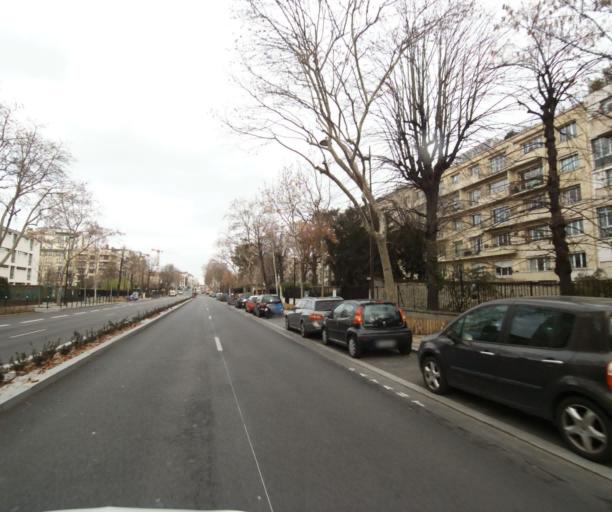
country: FR
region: Ile-de-France
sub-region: Departement des Hauts-de-Seine
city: Neuilly-sur-Seine
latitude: 48.8912
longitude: 2.2700
